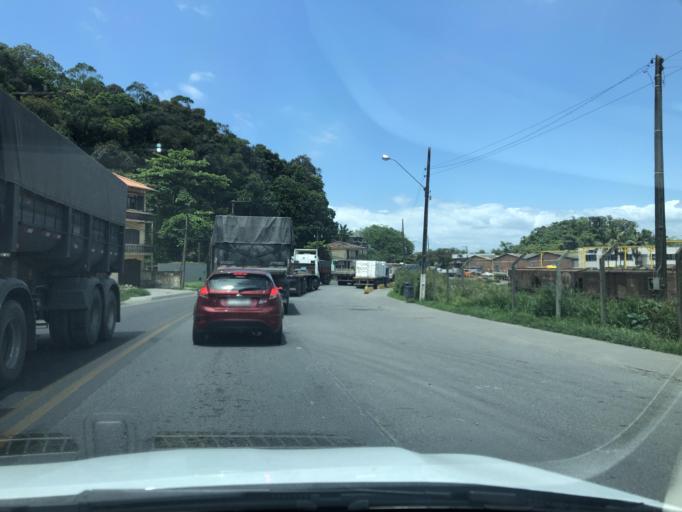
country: BR
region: Santa Catarina
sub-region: Sao Francisco Do Sul
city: Sao Francisco do Sul
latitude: -26.2406
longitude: -48.6327
